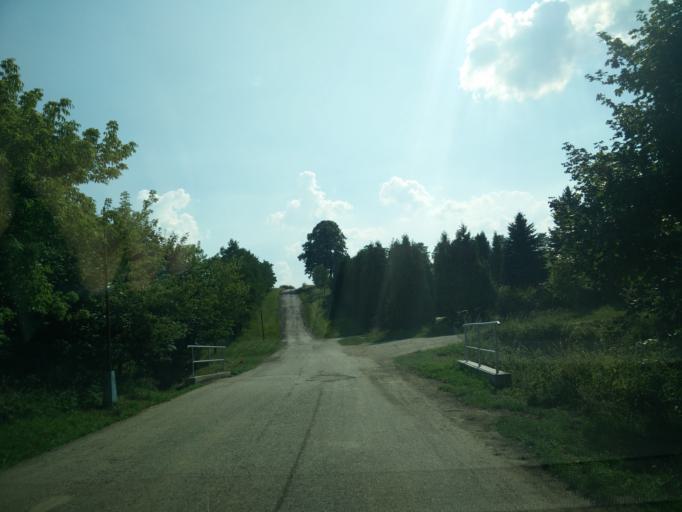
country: SK
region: Zilinsky
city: Rajec
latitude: 49.0597
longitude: 18.6509
